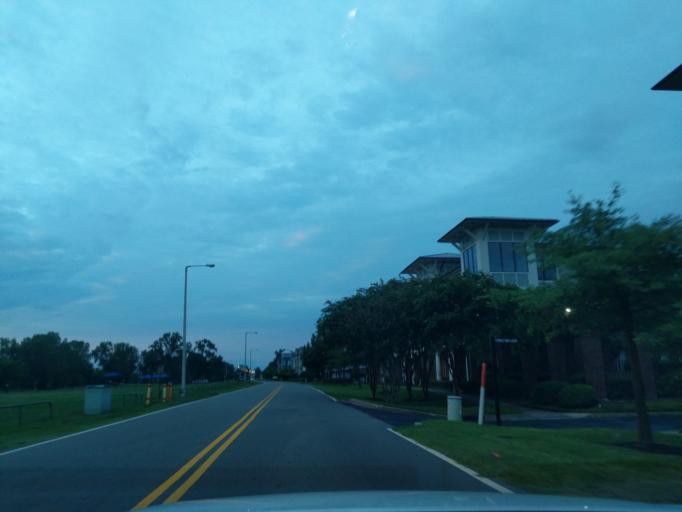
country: US
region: Tennessee
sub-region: Shelby County
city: Memphis
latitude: 35.1560
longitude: -90.0567
